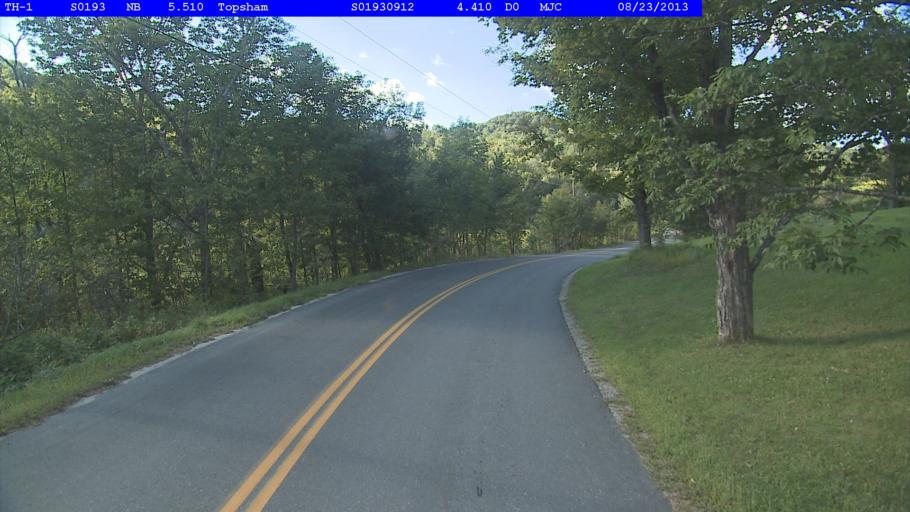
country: US
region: New Hampshire
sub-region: Grafton County
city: Haverhill
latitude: 44.1270
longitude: -72.2426
